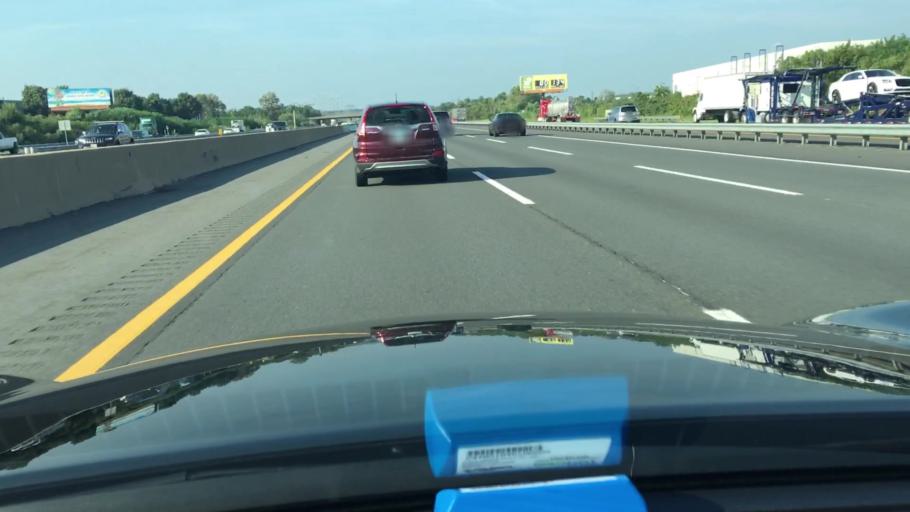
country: US
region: New Jersey
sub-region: Middlesex County
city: Jamesburg
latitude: 40.3678
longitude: -74.4656
